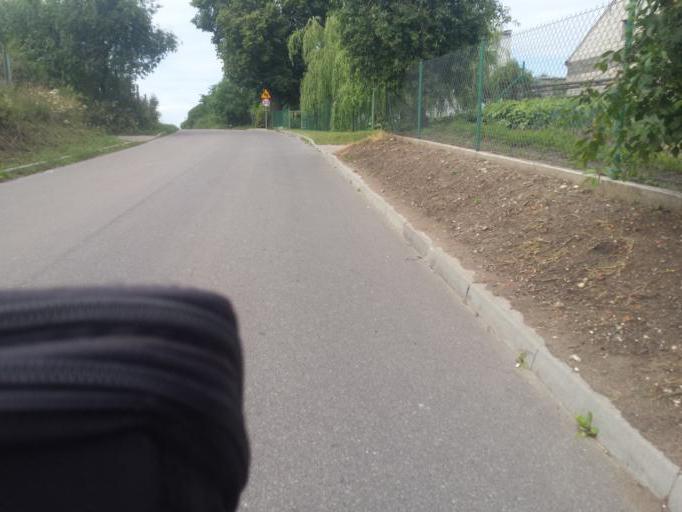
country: PL
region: Warmian-Masurian Voivodeship
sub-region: Powiat nowomiejski
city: Biskupiec
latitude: 53.5413
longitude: 19.4608
